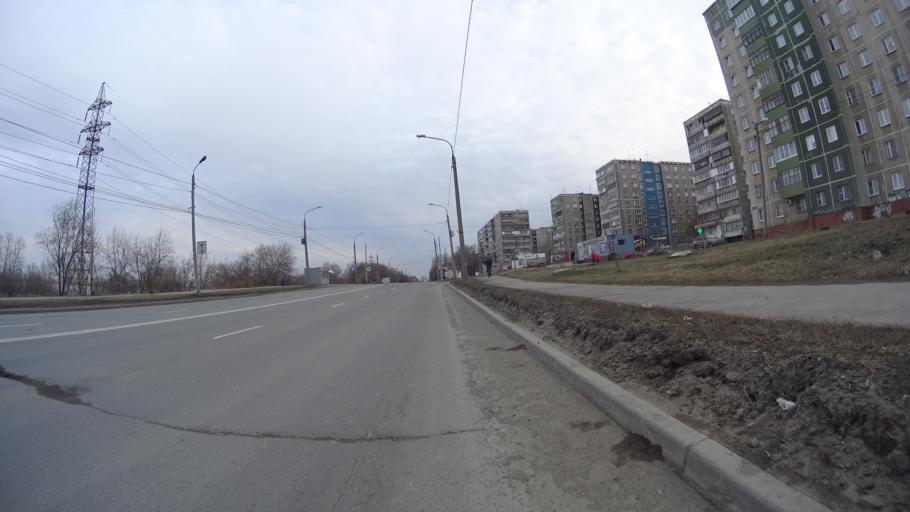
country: RU
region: Chelyabinsk
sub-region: Gorod Chelyabinsk
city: Chelyabinsk
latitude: 55.1852
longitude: 61.4848
